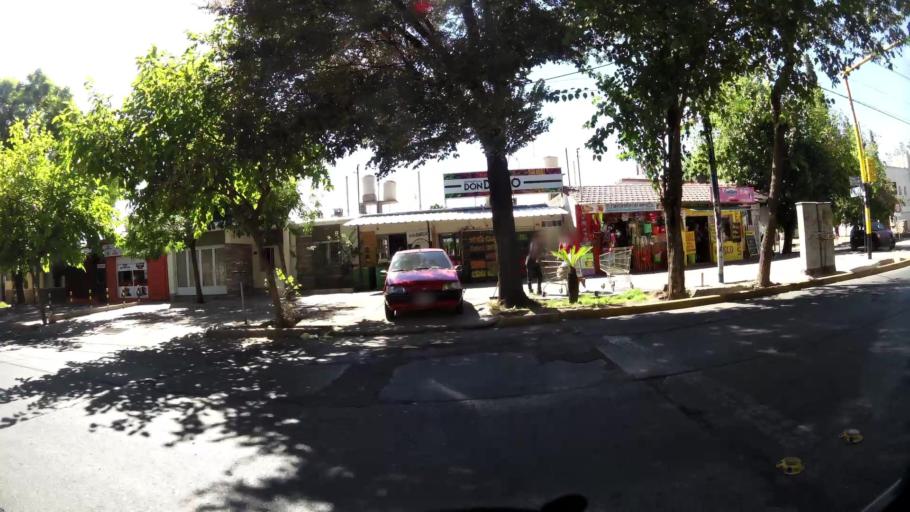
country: AR
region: Mendoza
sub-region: Departamento de Godoy Cruz
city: Godoy Cruz
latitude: -32.9162
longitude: -68.8594
